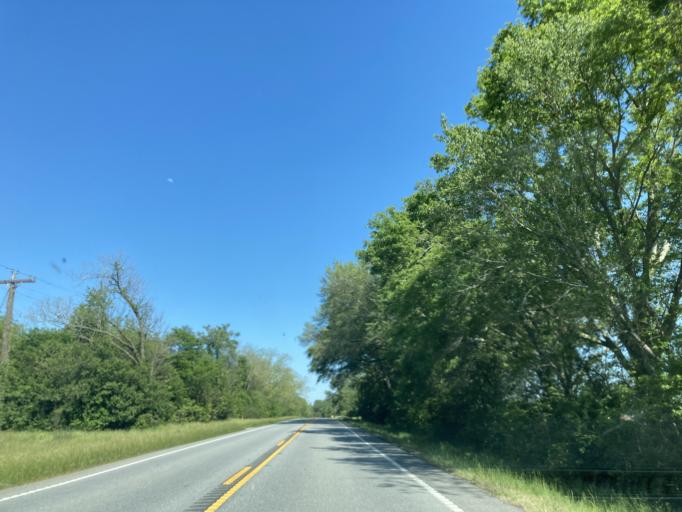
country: US
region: Georgia
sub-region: Miller County
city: Colquitt
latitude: 31.1834
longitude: -84.5477
